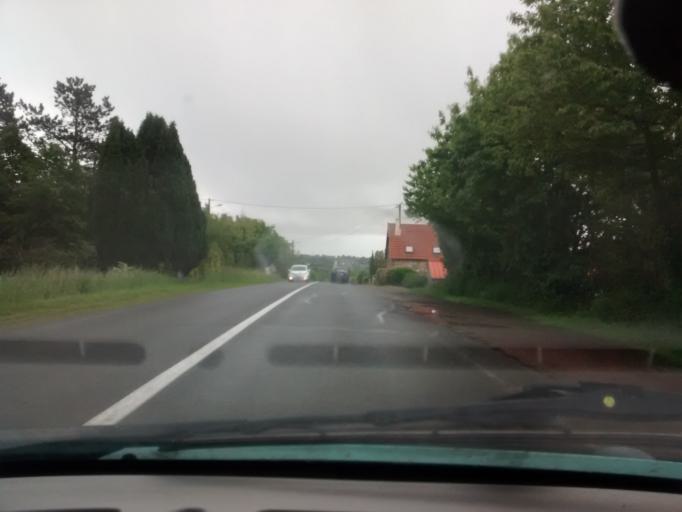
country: FR
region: Lower Normandy
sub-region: Departement de la Manche
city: Saint-Lo
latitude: 49.1006
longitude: -1.0607
